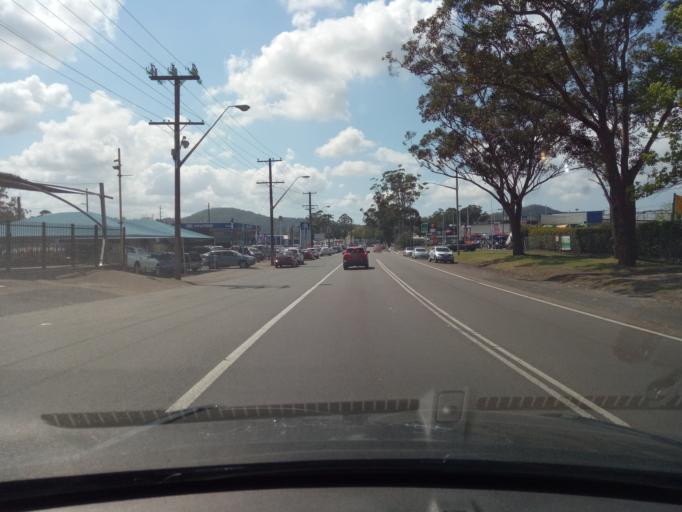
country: AU
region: New South Wales
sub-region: Gosford Shire
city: Gosford
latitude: -33.4119
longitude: 151.3454
